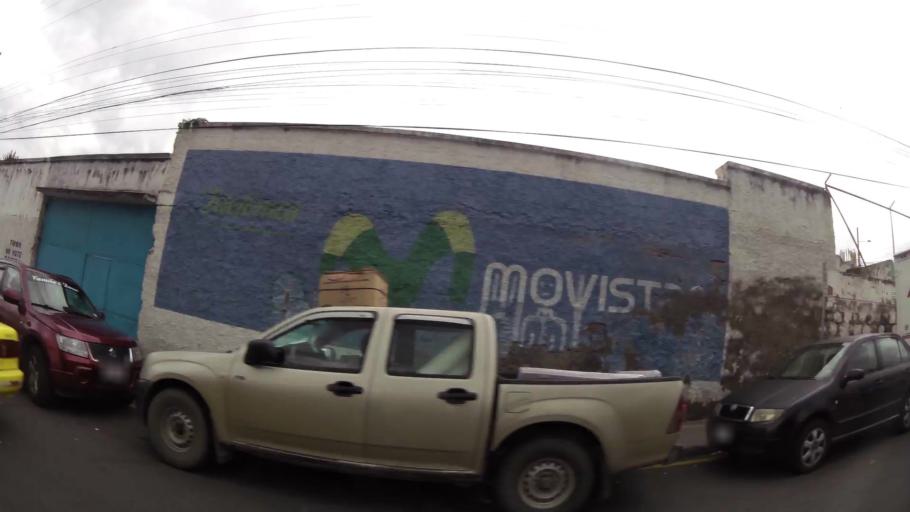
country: EC
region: Tungurahua
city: Ambato
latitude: -1.2357
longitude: -78.6157
